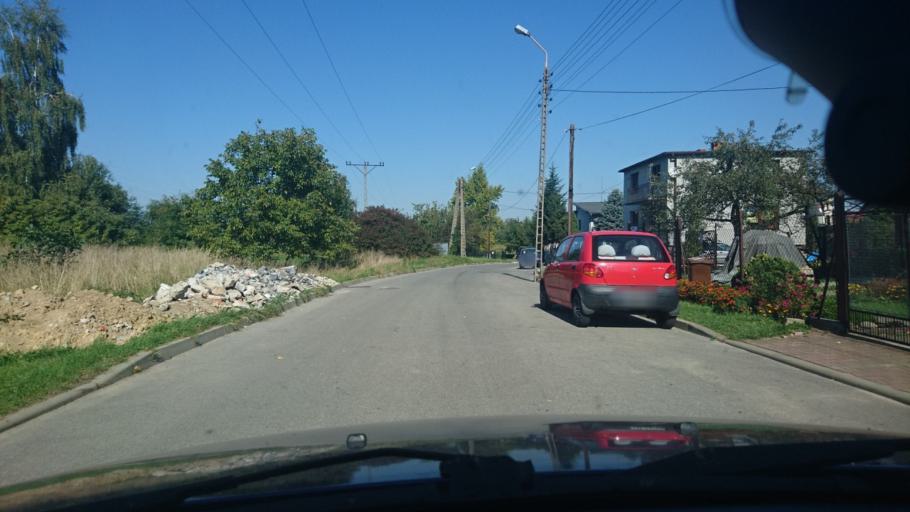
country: PL
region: Silesian Voivodeship
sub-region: Bielsko-Biala
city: Bielsko-Biala
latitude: 49.8437
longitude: 19.0621
